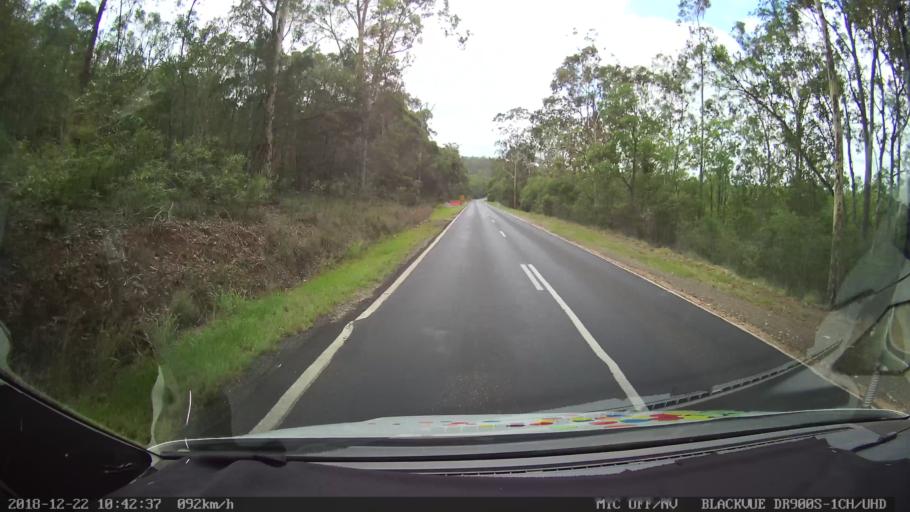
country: AU
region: New South Wales
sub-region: Clarence Valley
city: South Grafton
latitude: -29.6394
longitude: 152.7779
